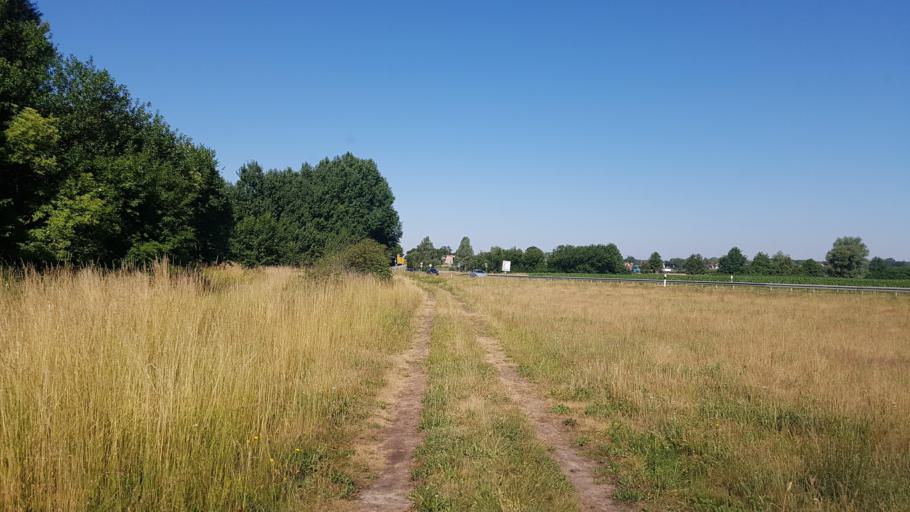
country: DE
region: Brandenburg
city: Juterbog
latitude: 51.9828
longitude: 13.1154
